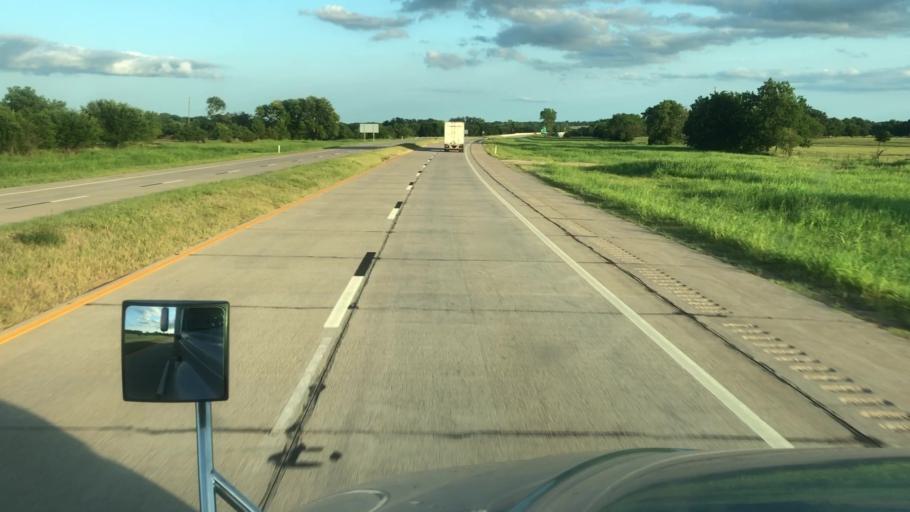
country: US
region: Oklahoma
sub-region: Pawnee County
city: Pawnee
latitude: 36.3163
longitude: -96.9948
